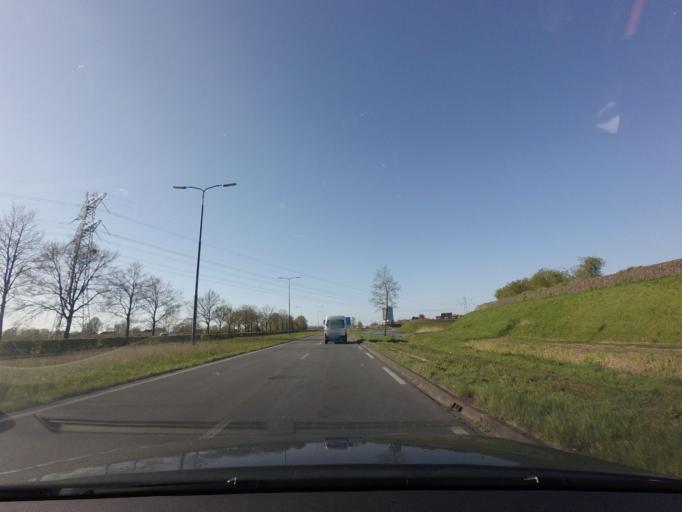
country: NL
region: Utrecht
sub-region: Gemeente Amersfoort
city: Hoogland
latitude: 52.1976
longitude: 5.3664
